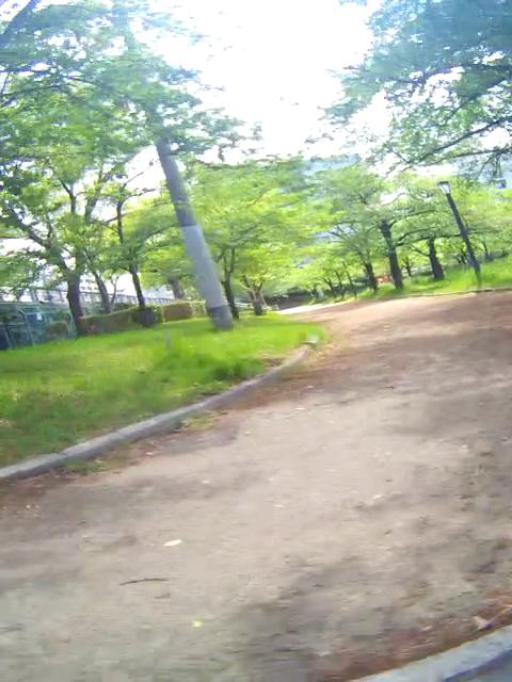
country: JP
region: Osaka
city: Osaka-shi
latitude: 34.7078
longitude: 135.5189
